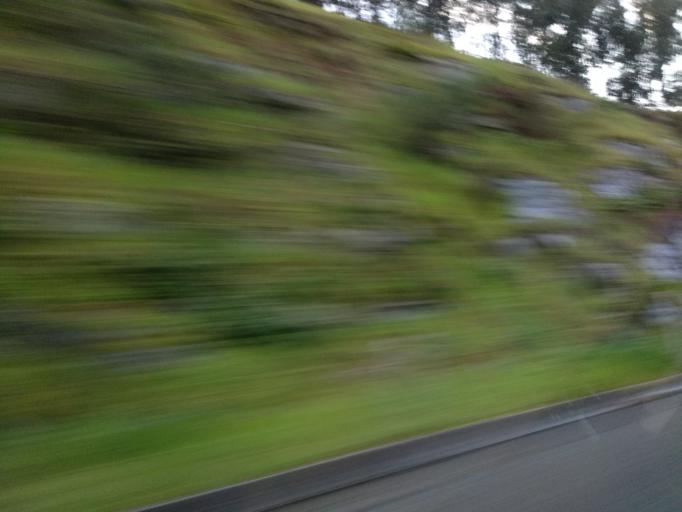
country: PT
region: Braga
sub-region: Braga
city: Oliveira
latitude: 41.4839
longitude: -8.4649
